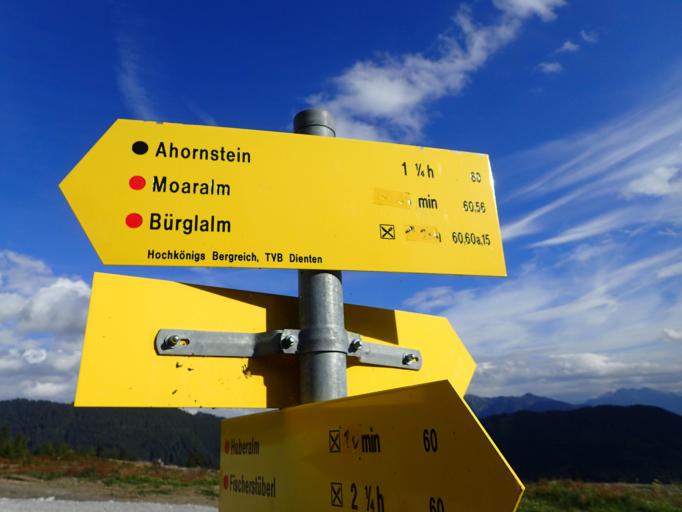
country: AT
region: Salzburg
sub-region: Politischer Bezirk Zell am See
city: Dienten am Hochkonig
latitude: 47.3547
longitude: 13.0320
